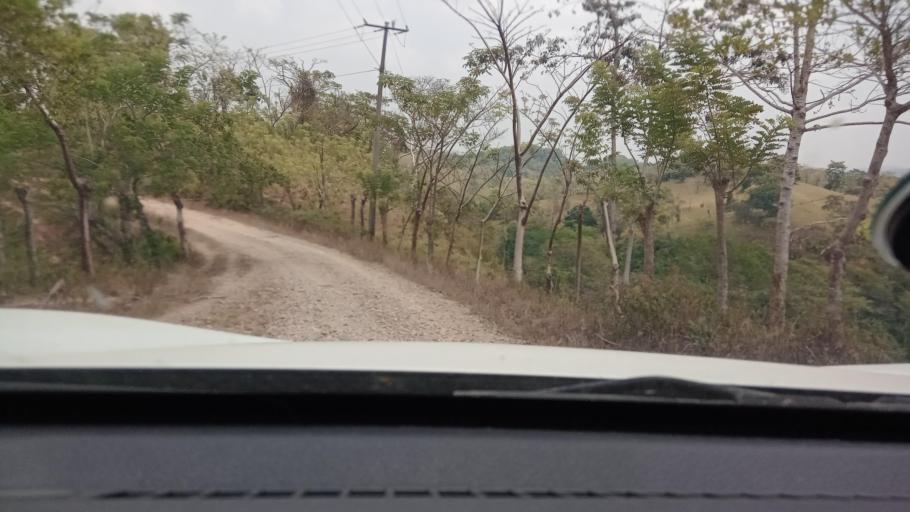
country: MX
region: Tabasco
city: Chontalpa
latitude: 17.5582
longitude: -93.7201
